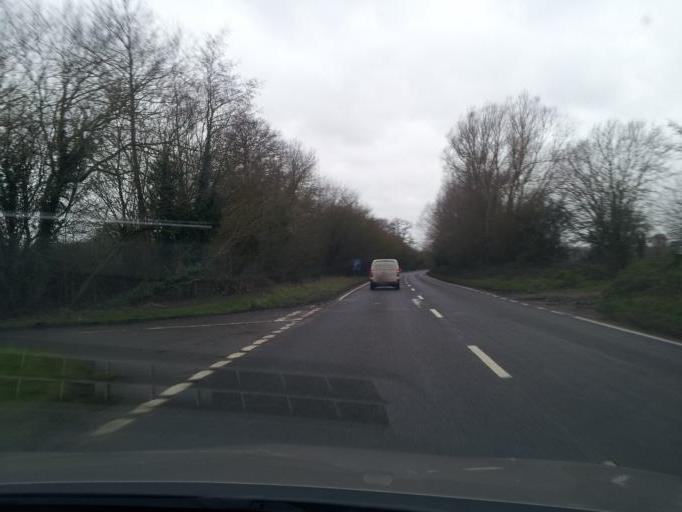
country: GB
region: England
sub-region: Suffolk
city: Botesdale
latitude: 52.3480
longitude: 1.0483
